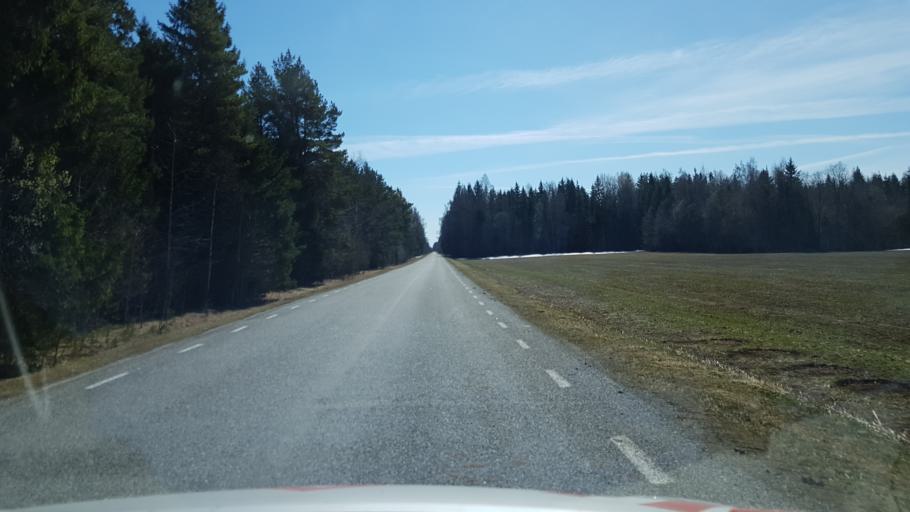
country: EE
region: Laeaene-Virumaa
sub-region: Vinni vald
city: Vinni
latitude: 59.1729
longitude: 26.5061
